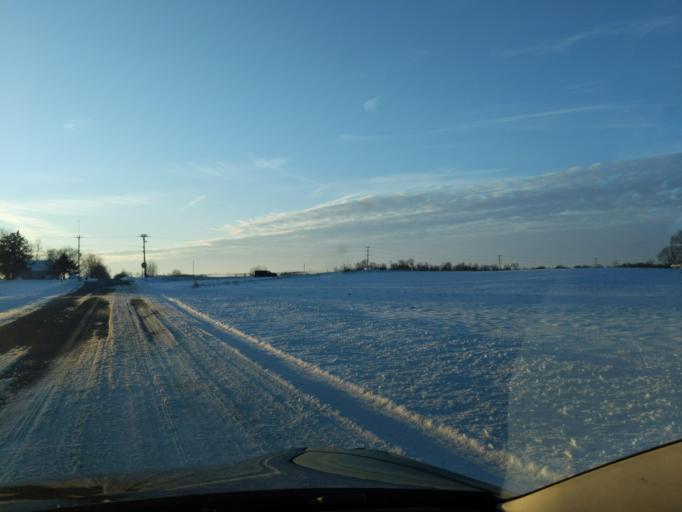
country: US
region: Michigan
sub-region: Ingham County
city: Webberville
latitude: 42.5696
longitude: -84.1907
